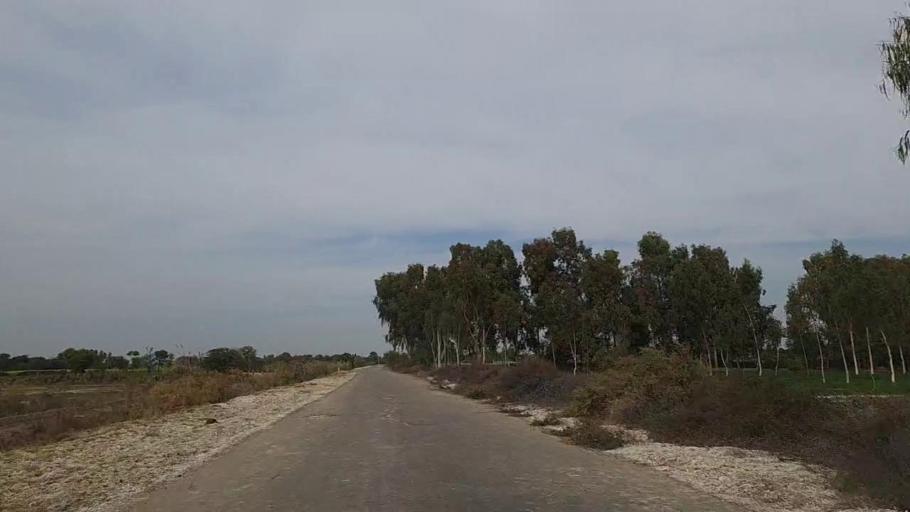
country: PK
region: Sindh
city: Daur
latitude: 26.4252
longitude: 68.4809
